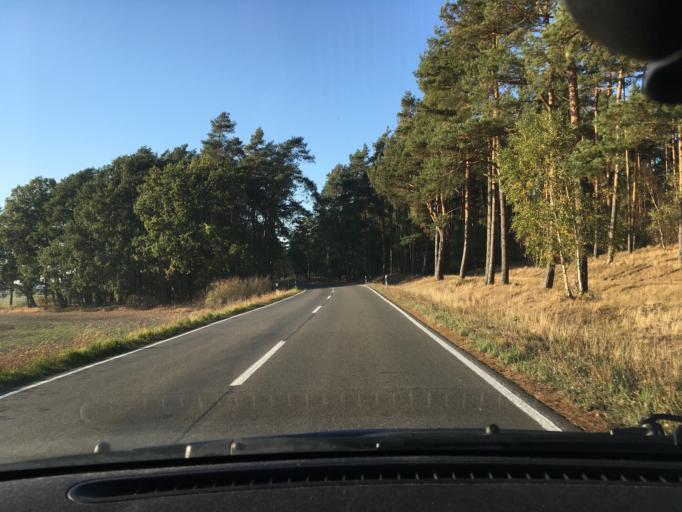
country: DE
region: Lower Saxony
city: Neu Darchau
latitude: 53.2706
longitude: 10.9466
